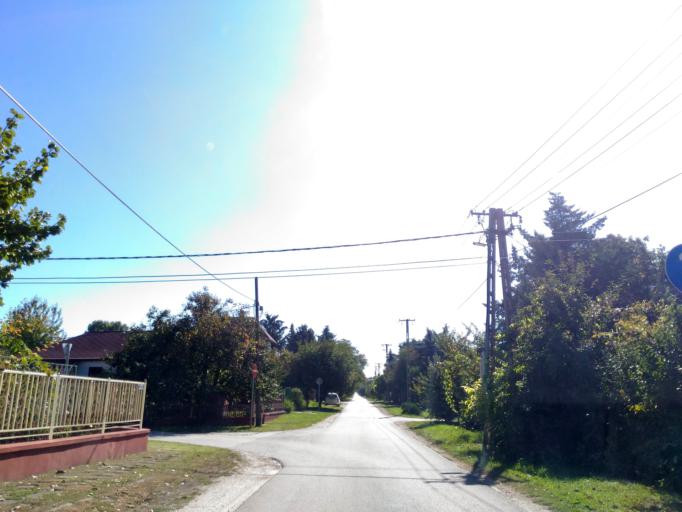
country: HU
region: Fejer
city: Gardony
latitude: 47.2099
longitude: 18.6387
